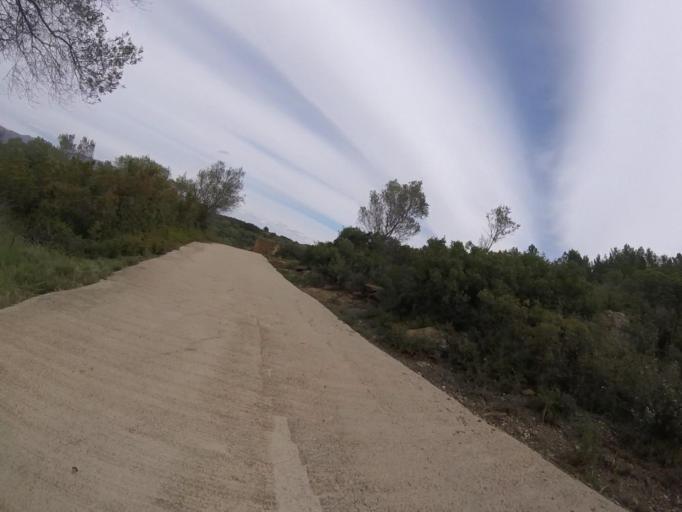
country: ES
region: Valencia
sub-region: Provincia de Castello
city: Cabanes
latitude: 40.1931
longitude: 0.0770
